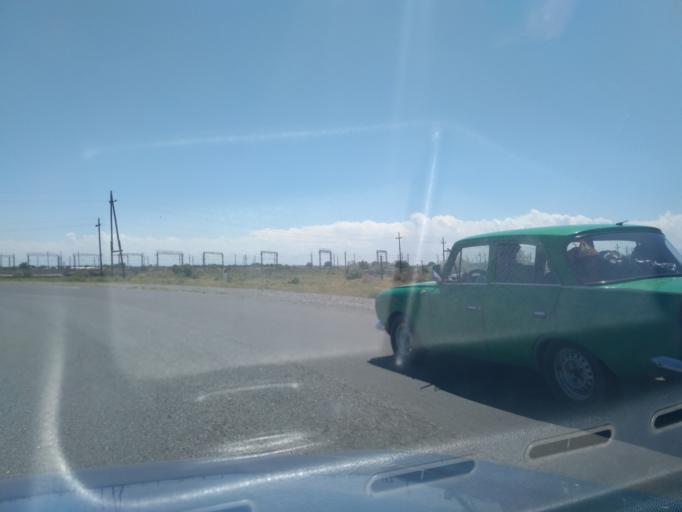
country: TJ
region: Viloyati Sughd
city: Zafarobod
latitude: 40.2133
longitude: 68.8579
